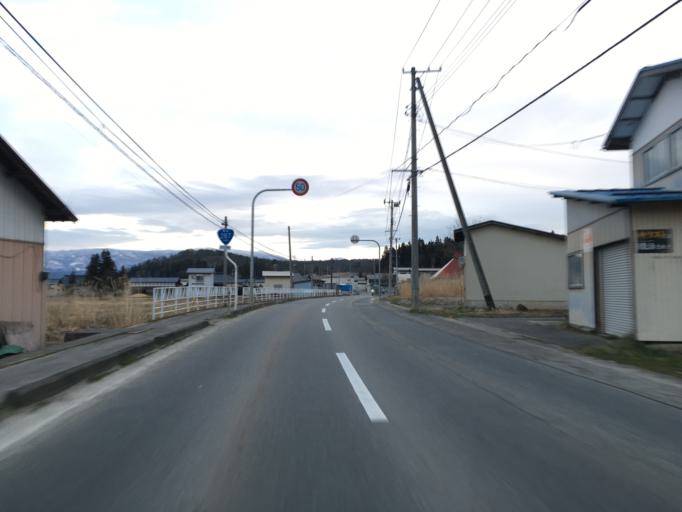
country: JP
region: Yamagata
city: Yonezawa
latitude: 37.9532
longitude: 140.0689
